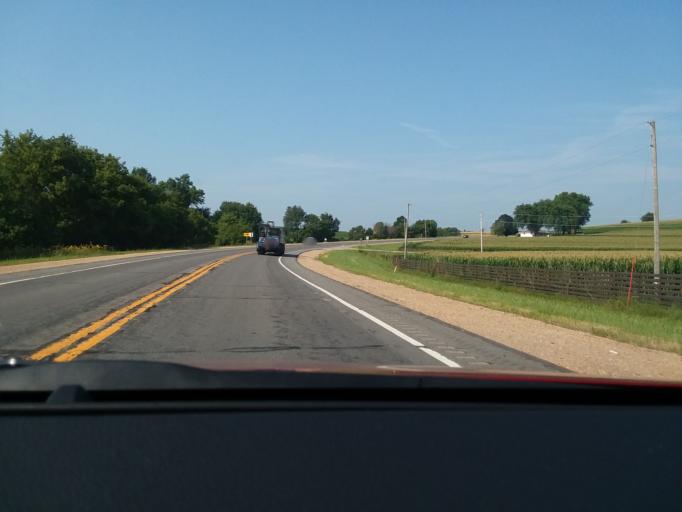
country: US
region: Wisconsin
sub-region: Dane County
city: Windsor
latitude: 43.1936
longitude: -89.3854
